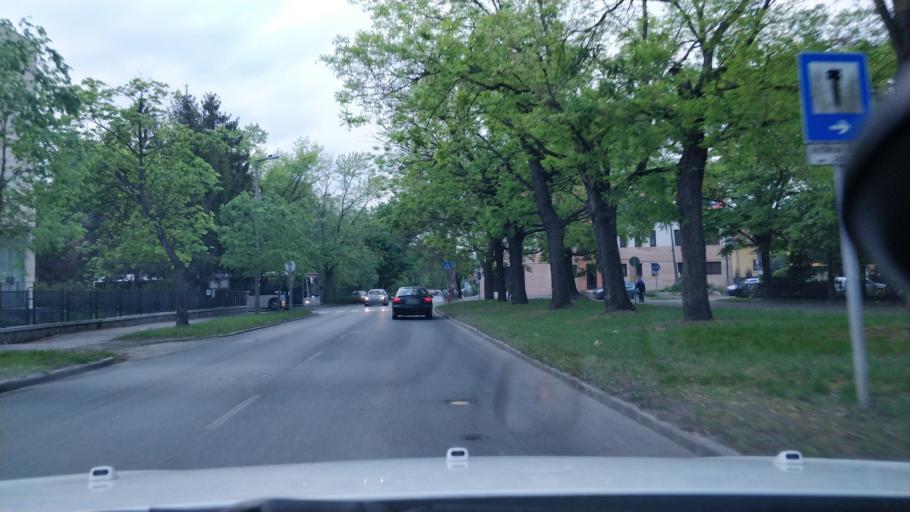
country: HU
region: Bacs-Kiskun
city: Kecskemet
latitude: 46.9092
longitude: 19.6787
